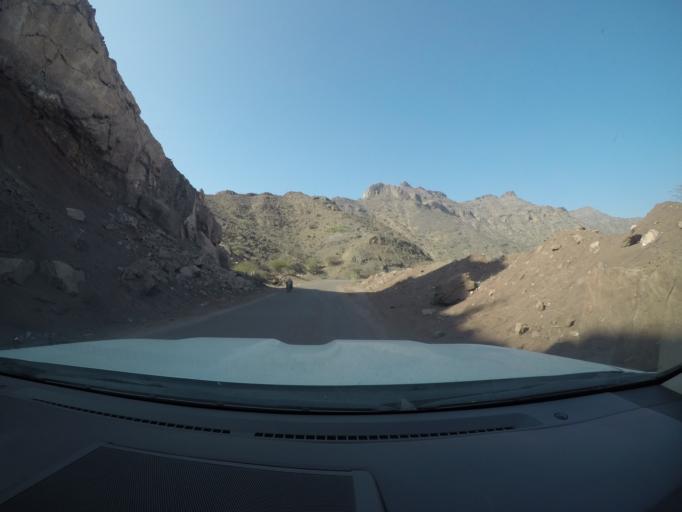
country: YE
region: Ad Dali'
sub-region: Ad Dhale'e
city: Dhalie
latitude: 13.6689
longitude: 44.7800
